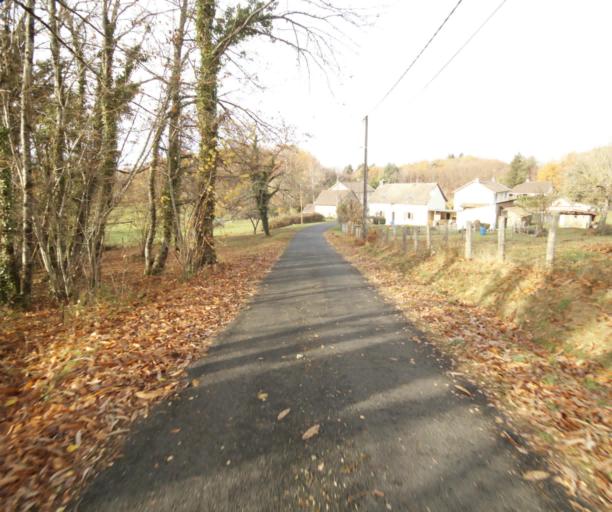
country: FR
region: Limousin
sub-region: Departement de la Correze
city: Sainte-Fortunade
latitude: 45.1680
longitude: 1.7475
